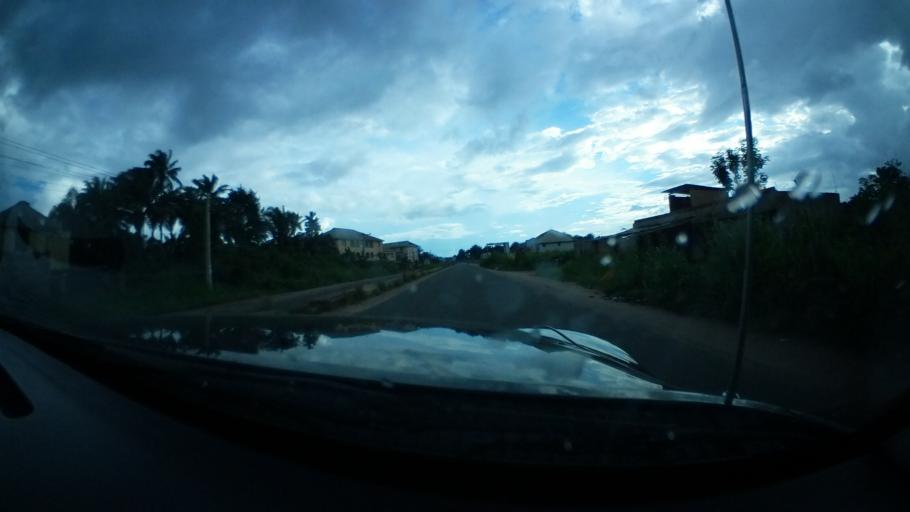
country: NG
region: Imo
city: Orlu
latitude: 5.7914
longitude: 7.0175
